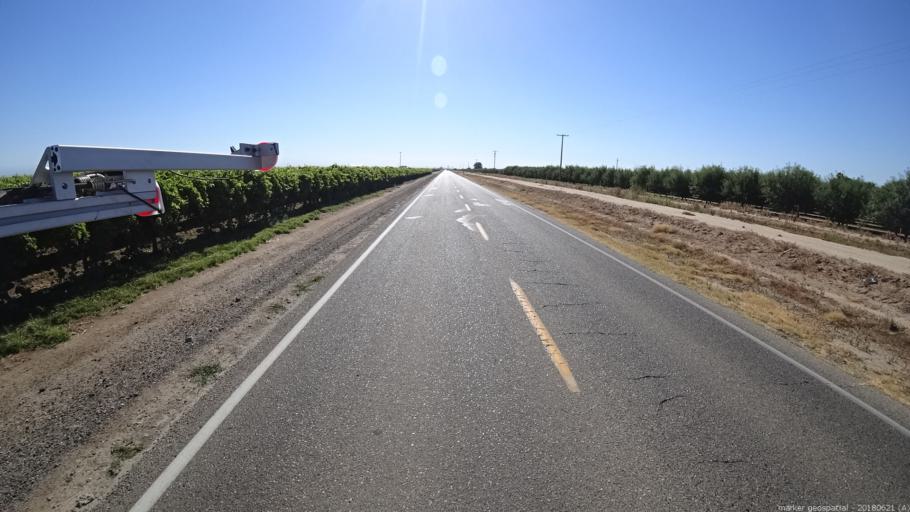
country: US
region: California
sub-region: Fresno County
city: Biola
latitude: 36.8512
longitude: -119.9804
